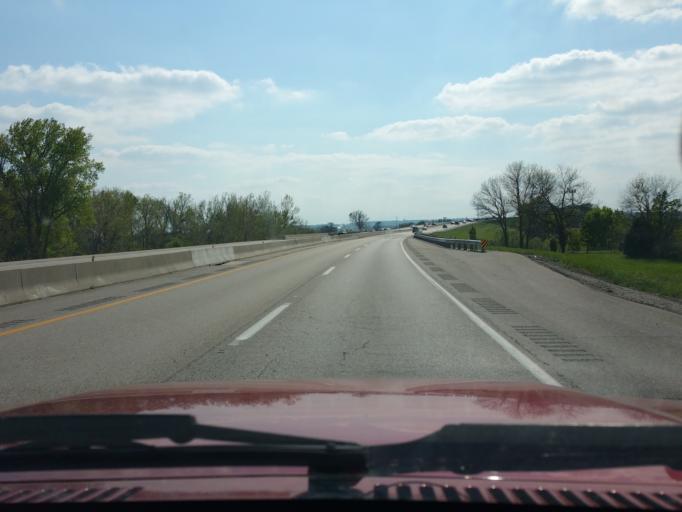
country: US
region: Kansas
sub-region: Douglas County
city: Lawrence
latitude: 38.9990
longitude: -95.1809
